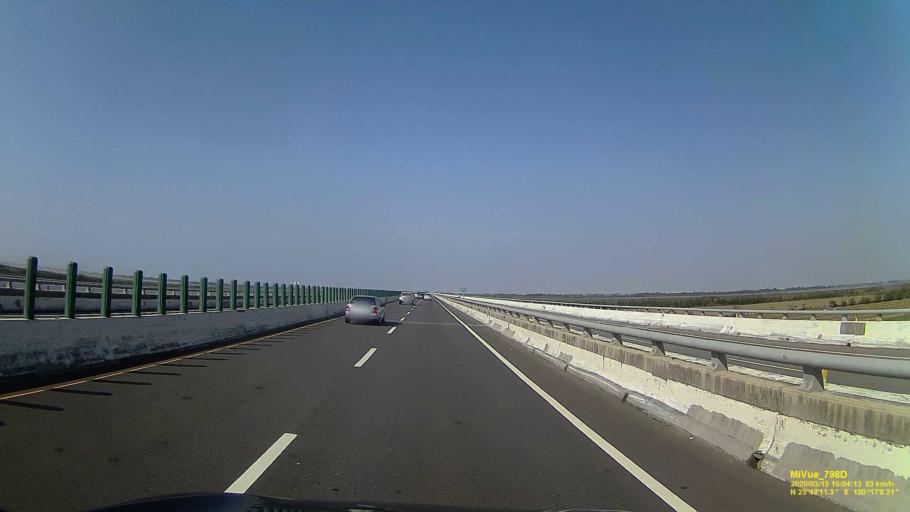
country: TW
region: Taiwan
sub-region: Yunlin
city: Douliu
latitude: 23.8204
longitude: 120.2859
